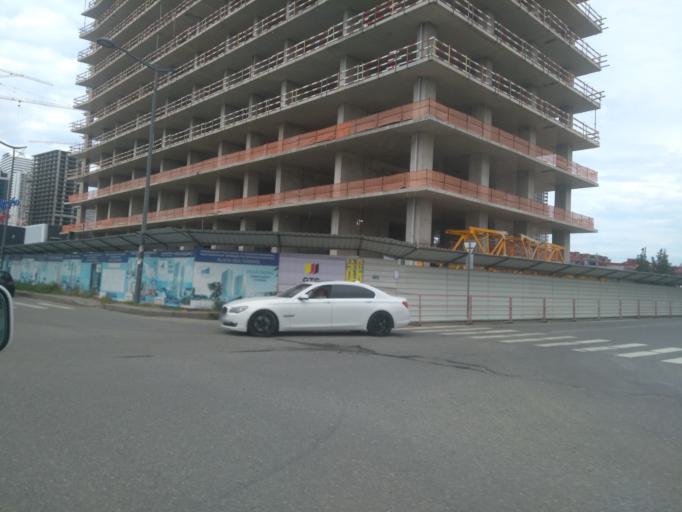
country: GE
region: Ajaria
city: Batumi
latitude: 41.6362
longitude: 41.6205
